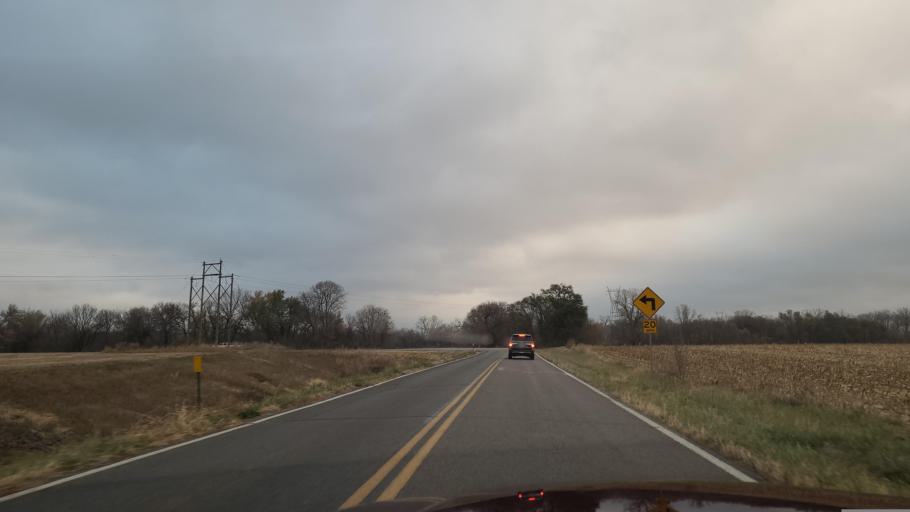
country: US
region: Kansas
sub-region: Douglas County
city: Lawrence
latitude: 38.9615
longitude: -95.2002
